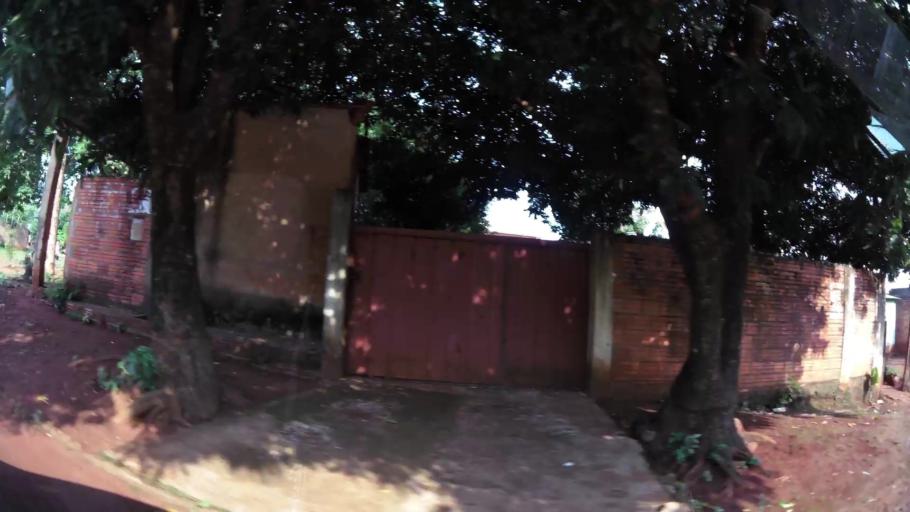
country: PY
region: Alto Parana
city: Ciudad del Este
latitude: -25.4881
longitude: -54.6504
